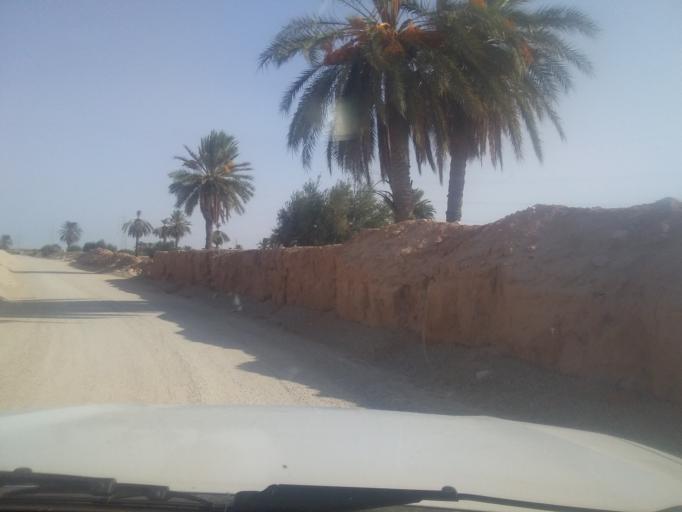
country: TN
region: Qabis
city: Matmata
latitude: 33.5895
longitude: 10.2673
